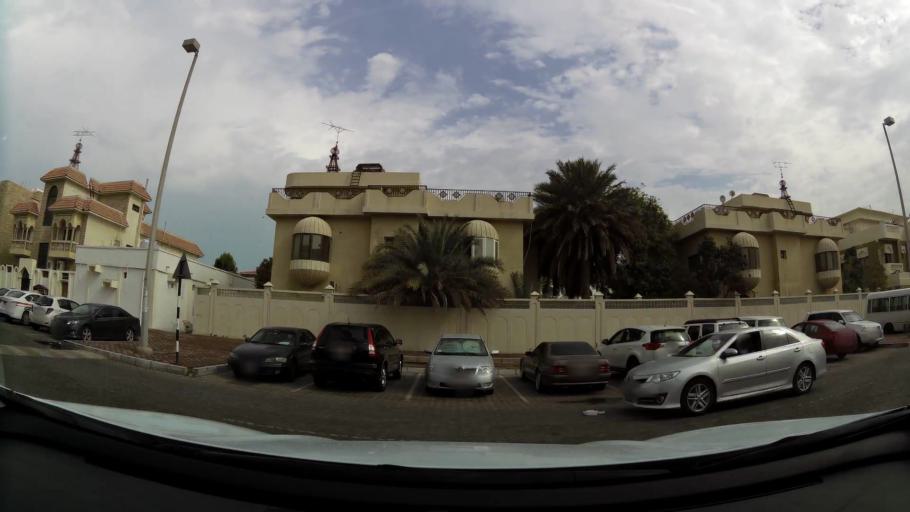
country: AE
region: Abu Dhabi
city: Abu Dhabi
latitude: 24.4399
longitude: 54.4134
